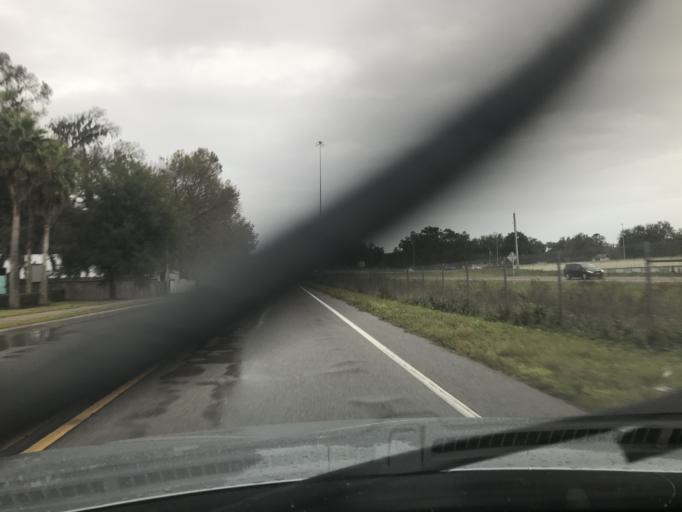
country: US
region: Florida
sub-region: Hillsborough County
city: Plant City
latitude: 28.0378
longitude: -82.1016
